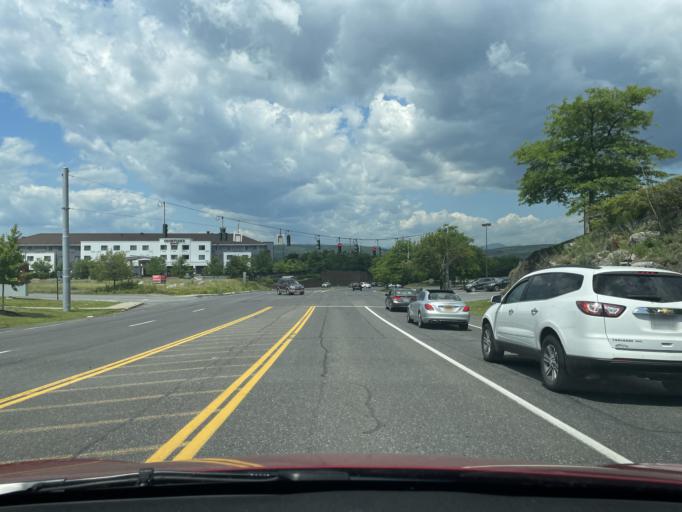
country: US
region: New York
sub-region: Ulster County
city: Lake Katrine
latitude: 41.9701
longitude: -73.9843
